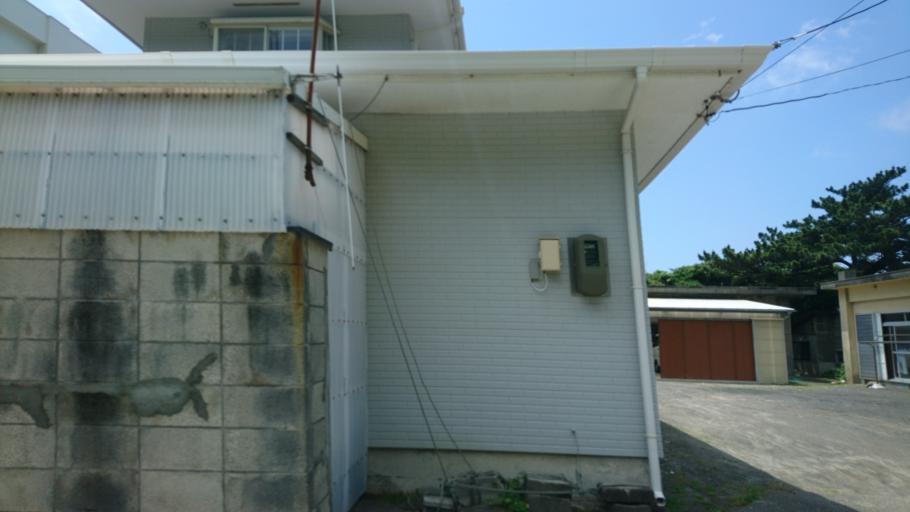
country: JP
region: Shizuoka
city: Shimoda
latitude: 34.4228
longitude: 139.2826
